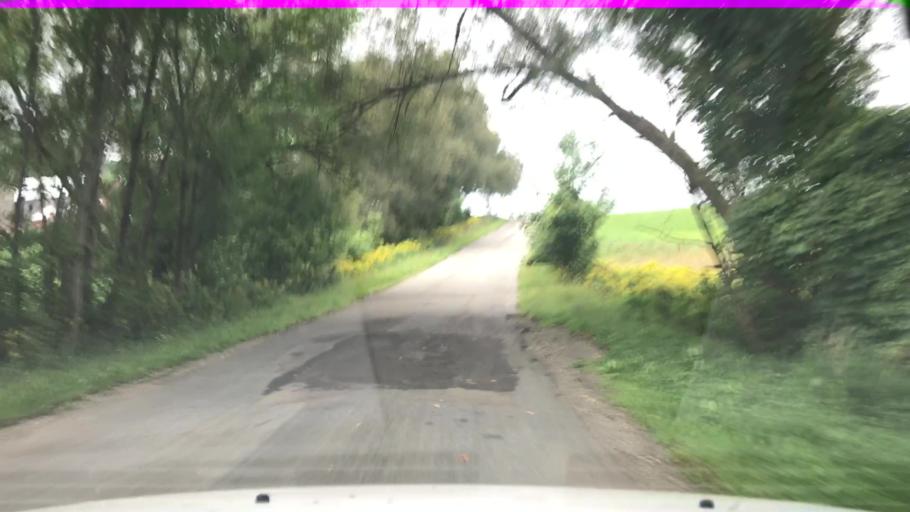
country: US
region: New York
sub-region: Cattaraugus County
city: Little Valley
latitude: 42.3204
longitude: -78.7234
